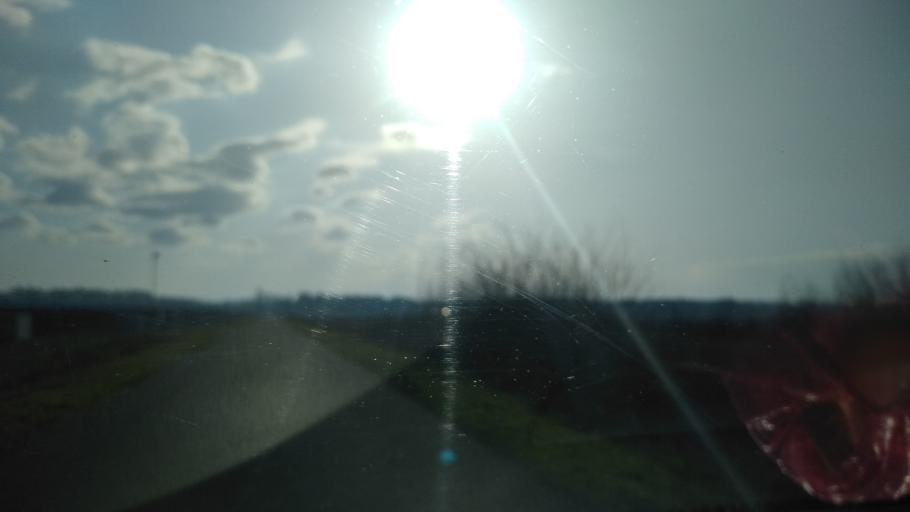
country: HU
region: Somogy
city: Barcs
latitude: 45.9707
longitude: 17.4973
